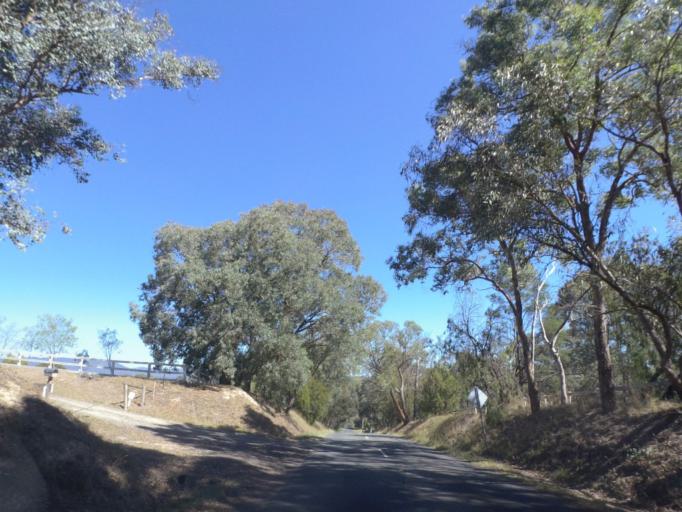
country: AU
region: Victoria
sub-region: Yarra Ranges
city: Chirnside Park
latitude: -37.7278
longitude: 145.2841
